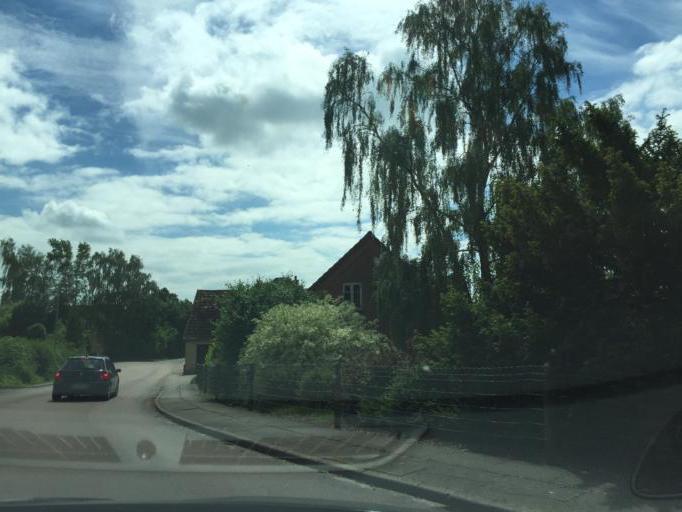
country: DK
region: South Denmark
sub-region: Faaborg-Midtfyn Kommune
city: Ringe
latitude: 55.2037
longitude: 10.4489
